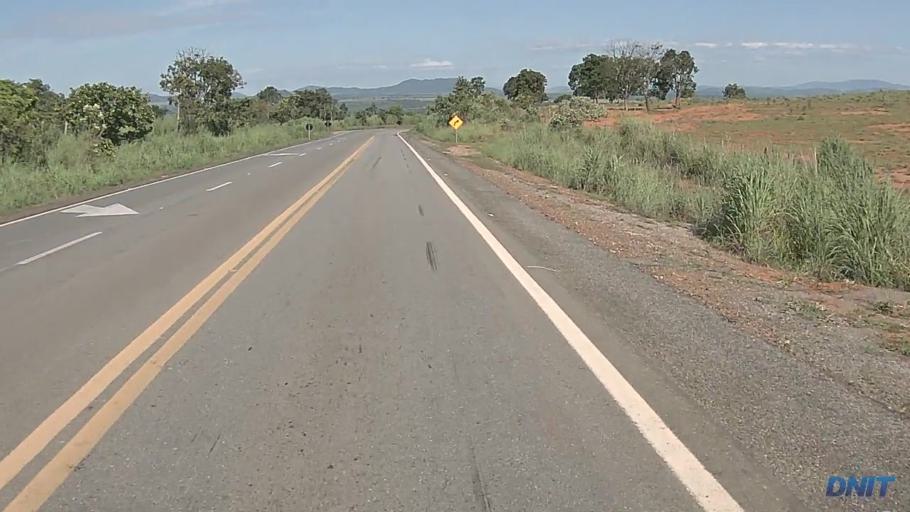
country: BR
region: Goias
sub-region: Padre Bernardo
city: Padre Bernardo
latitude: -15.2208
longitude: -48.5221
